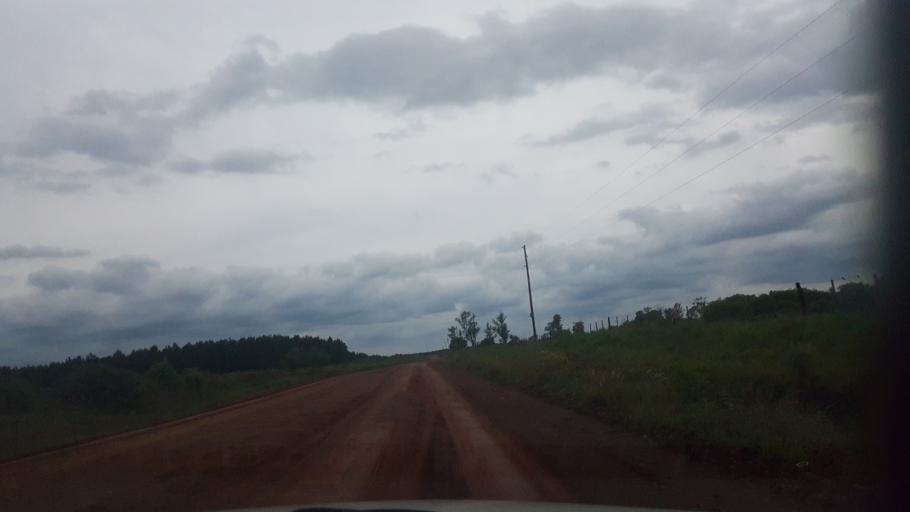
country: AR
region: Misiones
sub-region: Departamento de Candelaria
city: Candelaria
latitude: -27.4958
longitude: -55.7372
